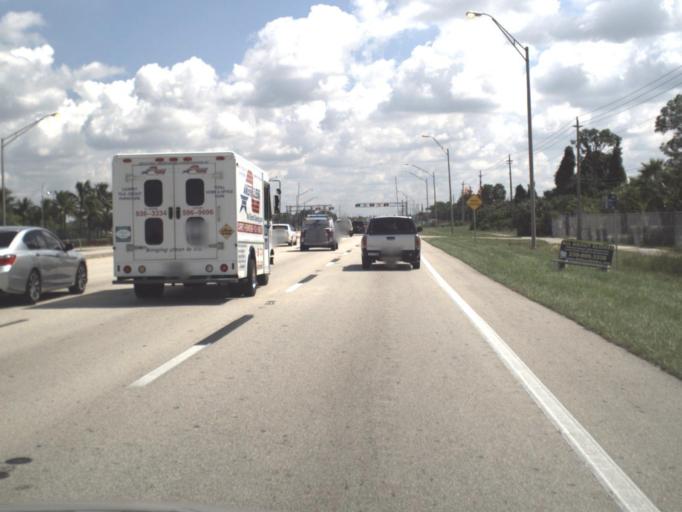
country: US
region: Florida
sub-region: Lee County
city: Fort Myers
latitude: 26.5972
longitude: -81.8579
